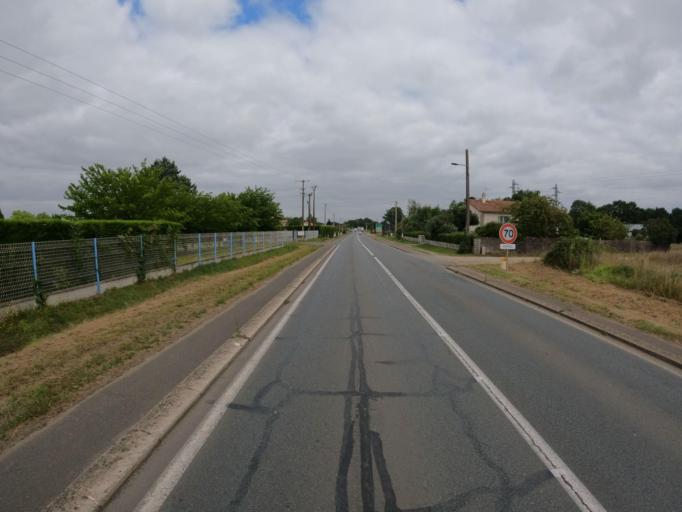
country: FR
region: Poitou-Charentes
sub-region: Departement des Deux-Sevres
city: Melle
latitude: 46.2131
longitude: -0.1440
